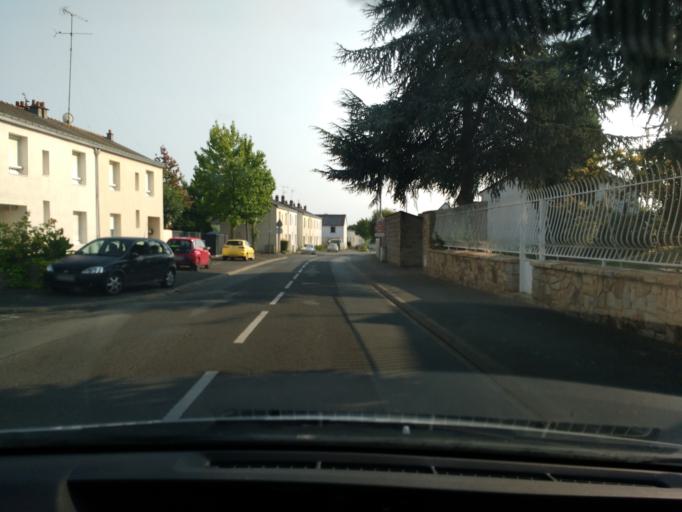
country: FR
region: Pays de la Loire
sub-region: Departement de Maine-et-Loire
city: Angers
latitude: 47.4685
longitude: -0.5079
